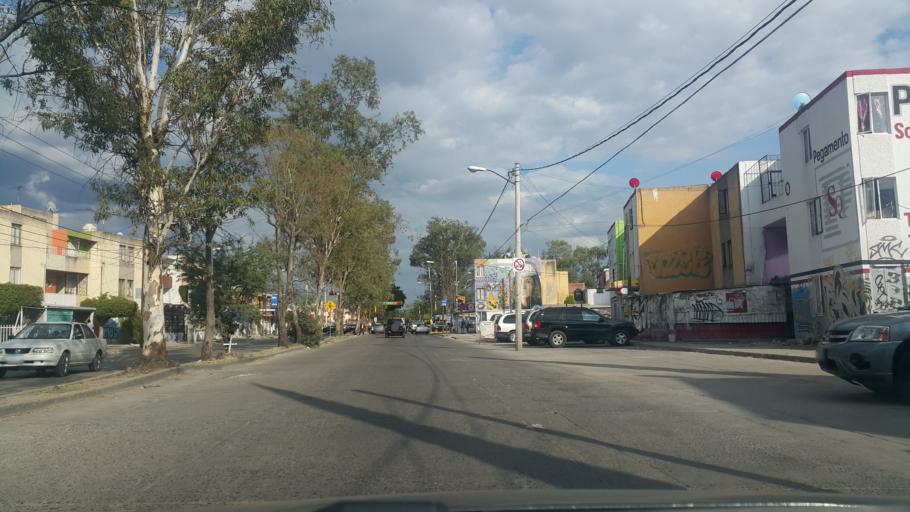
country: MX
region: Guanajuato
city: Leon
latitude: 21.1319
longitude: -101.6464
